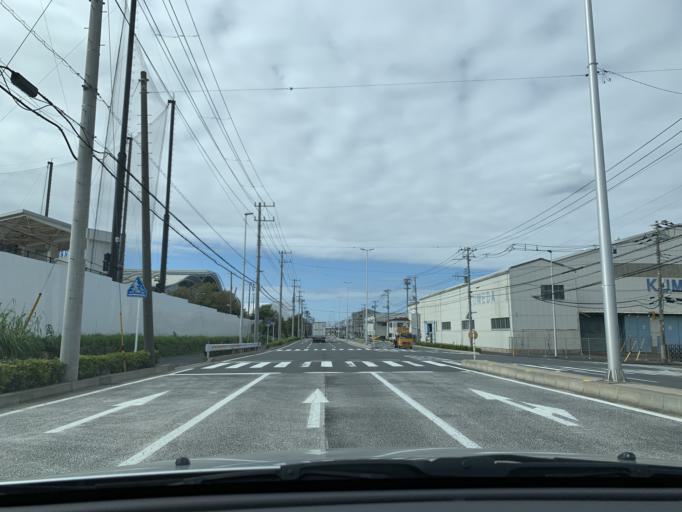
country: JP
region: Tokyo
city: Urayasu
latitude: 35.6292
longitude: 139.8945
